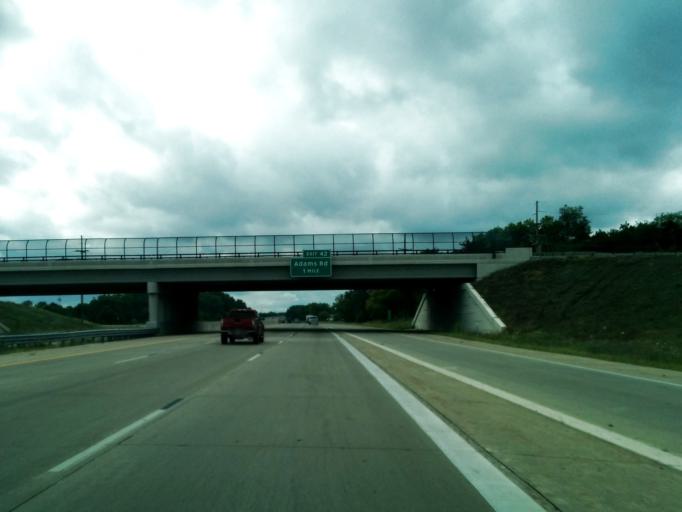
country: US
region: Michigan
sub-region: Oakland County
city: Rochester Hills
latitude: 42.6448
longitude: -83.1696
